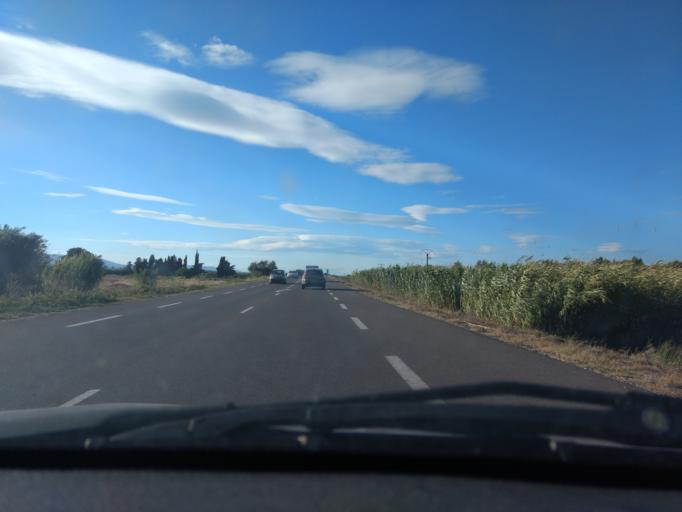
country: FR
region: Languedoc-Roussillon
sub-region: Departement des Pyrenees-Orientales
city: Le Barcares
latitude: 42.7673
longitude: 3.0182
